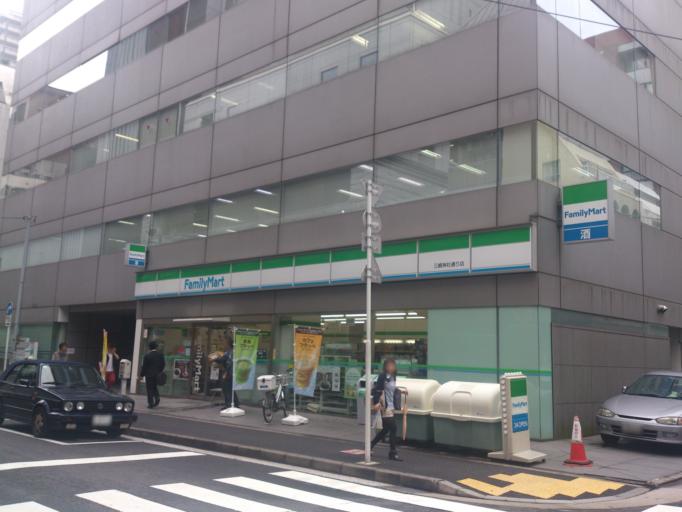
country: JP
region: Tokyo
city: Tokyo
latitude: 35.7009
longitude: 139.7546
